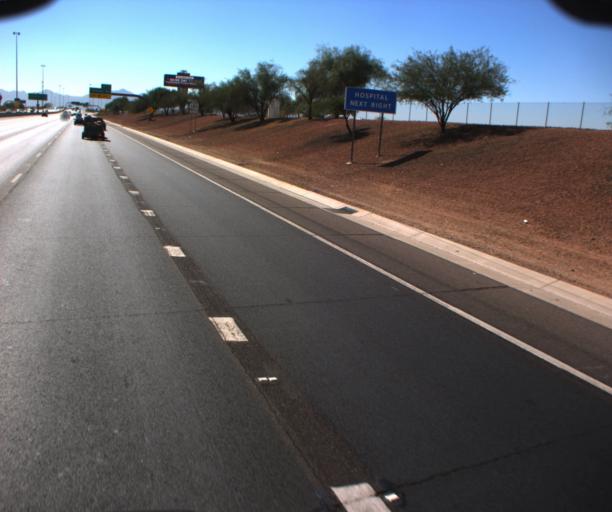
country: US
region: Arizona
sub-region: Maricopa County
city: Tolleson
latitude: 33.4892
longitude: -112.2640
